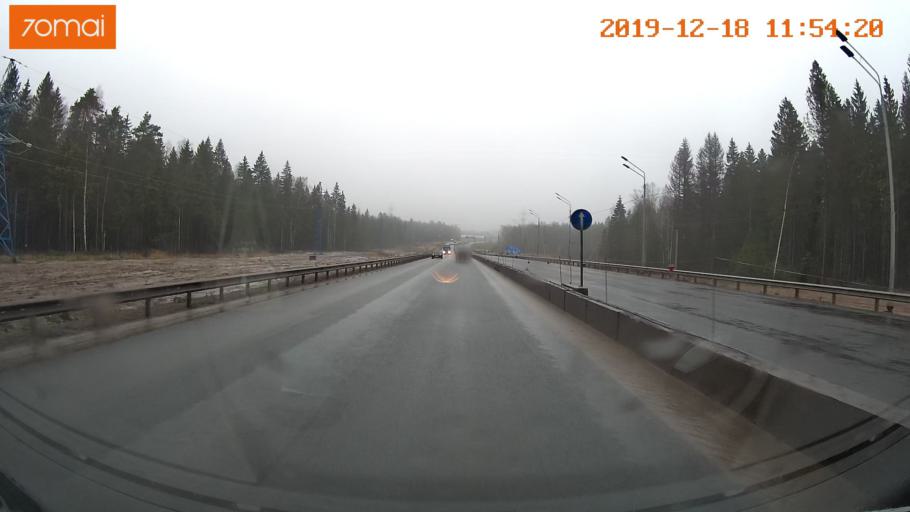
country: RU
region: Moskovskaya
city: Yershovo
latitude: 55.8145
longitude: 36.9180
